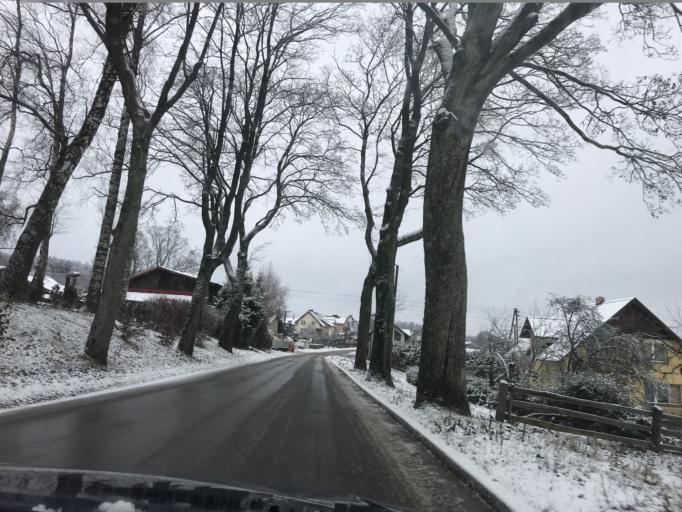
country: PL
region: Pomeranian Voivodeship
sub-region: Powiat bytowski
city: Bytow
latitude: 54.2156
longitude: 17.5614
